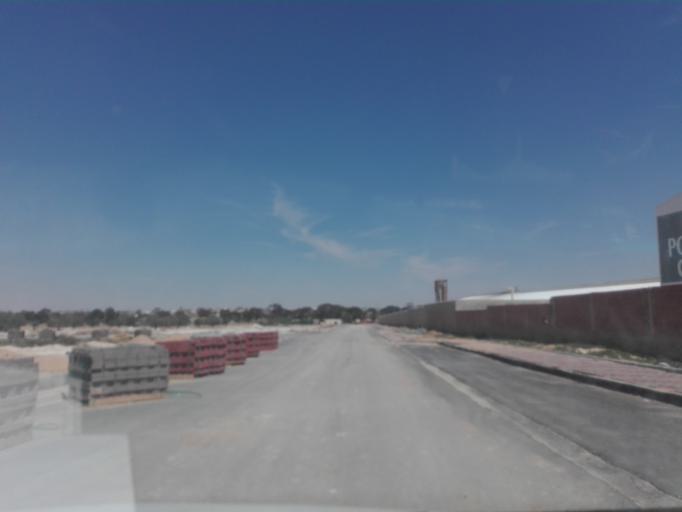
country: TN
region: Safaqis
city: Sfax
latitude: 34.7265
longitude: 10.5195
